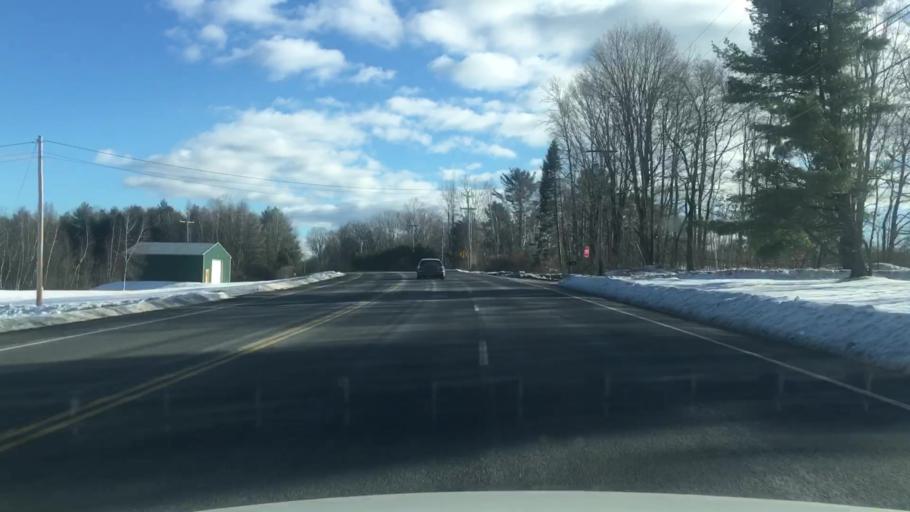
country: US
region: Maine
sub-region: Somerset County
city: Skowhegan
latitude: 44.8210
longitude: -69.7758
